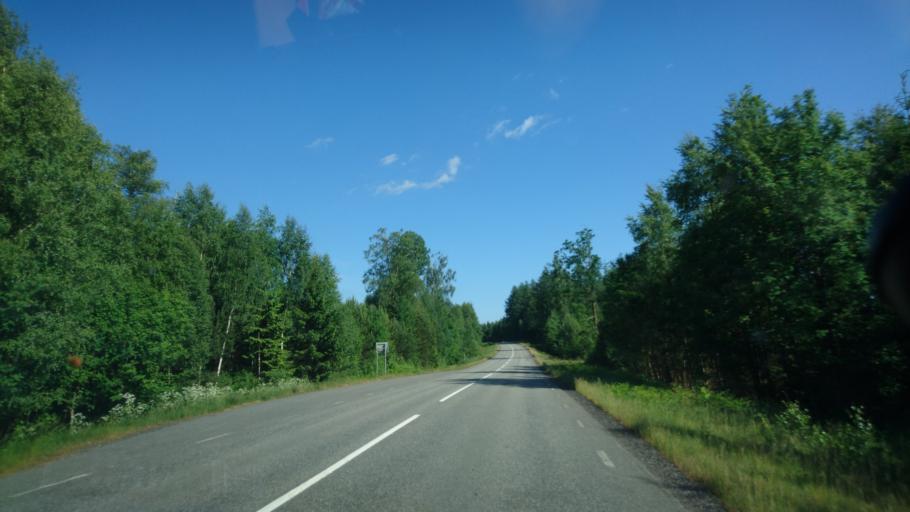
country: SE
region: Skane
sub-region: Osby Kommun
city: Lonsboda
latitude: 56.4336
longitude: 14.2585
